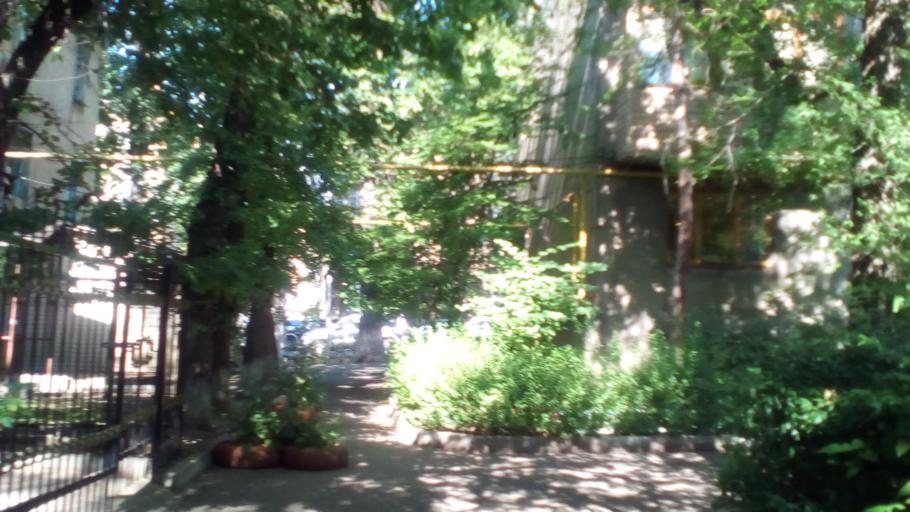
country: KZ
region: Almaty Qalasy
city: Almaty
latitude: 43.2489
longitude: 76.9398
